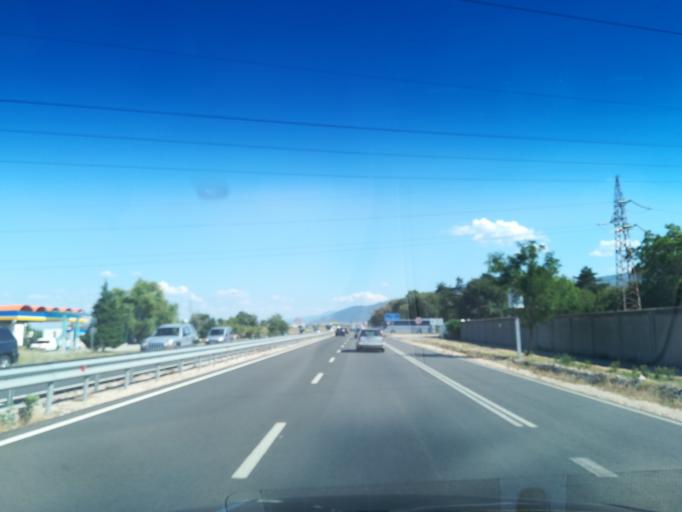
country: BG
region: Plovdiv
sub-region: Obshtina Asenovgrad
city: Asenovgrad
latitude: 42.0643
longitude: 24.8176
